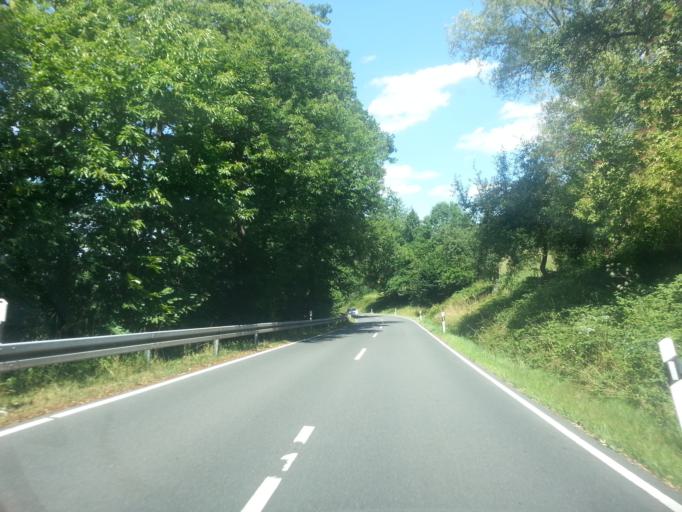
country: DE
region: Hesse
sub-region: Regierungsbezirk Darmstadt
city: Frankisch-Crumbach
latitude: 49.7226
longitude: 8.8691
